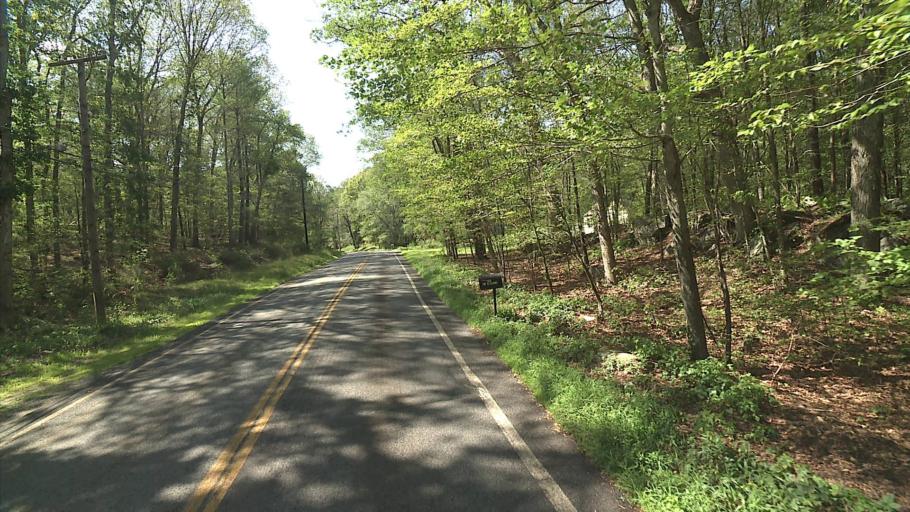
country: US
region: Connecticut
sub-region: Tolland County
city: Mansfield City
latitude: 41.8043
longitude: -72.1718
